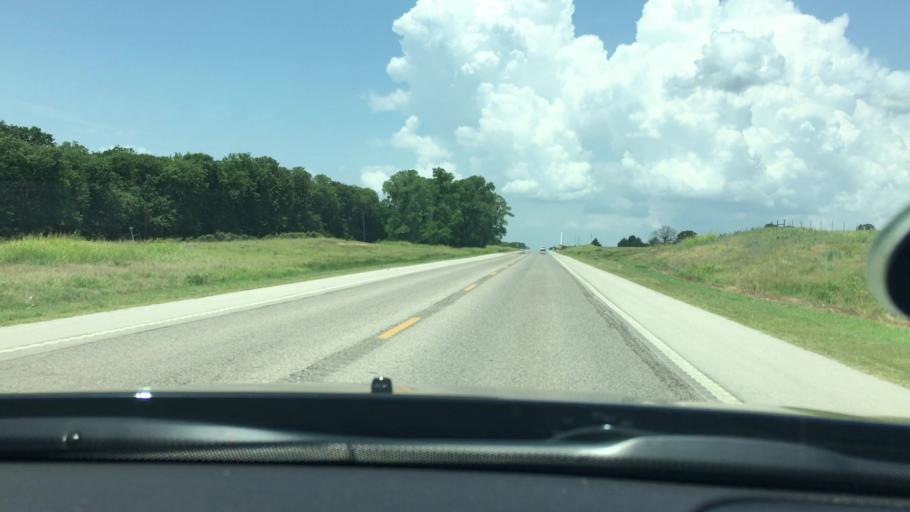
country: US
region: Oklahoma
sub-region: Carter County
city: Dickson
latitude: 34.1003
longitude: -96.9270
